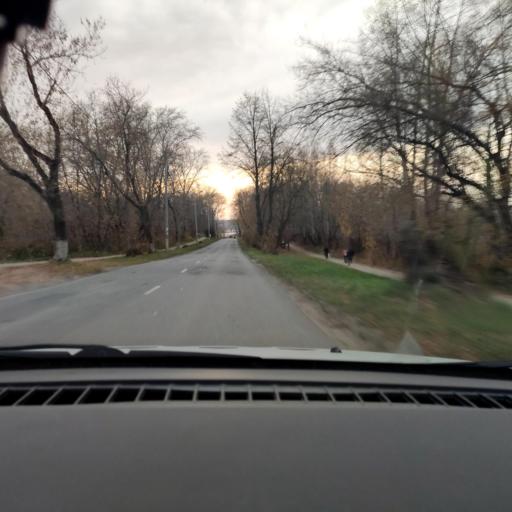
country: RU
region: Perm
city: Perm
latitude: 58.1210
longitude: 56.3760
